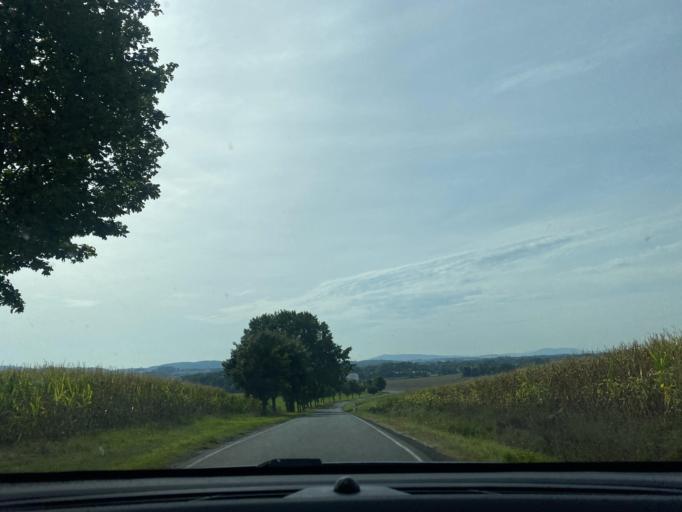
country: DE
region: Saxony
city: Quitzdorf
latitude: 51.2286
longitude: 14.7743
